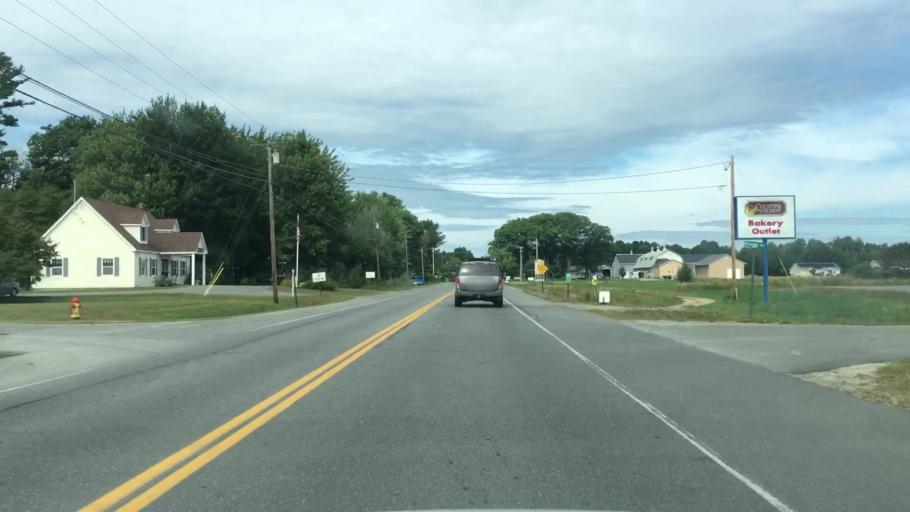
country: US
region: Maine
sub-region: Piscataquis County
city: Milo
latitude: 45.2640
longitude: -68.9916
